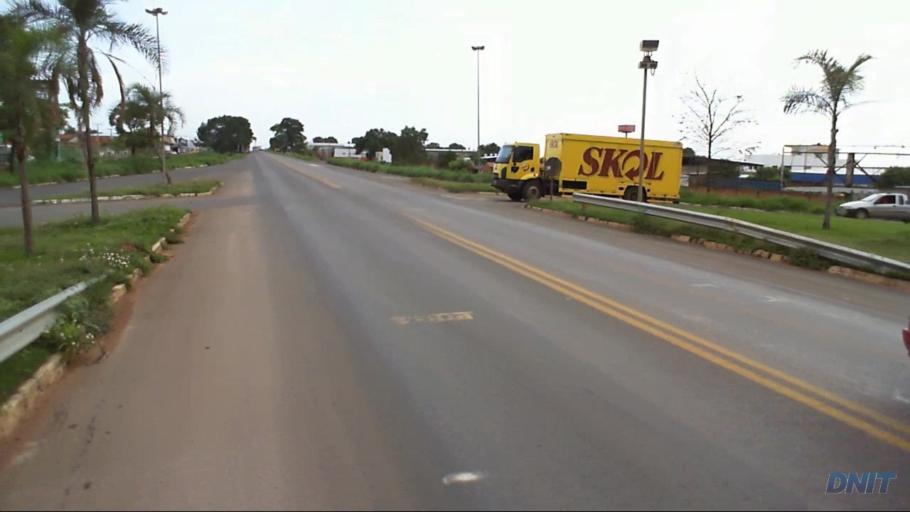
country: BR
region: Goias
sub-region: Uruacu
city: Uruacu
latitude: -14.5330
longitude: -49.1609
